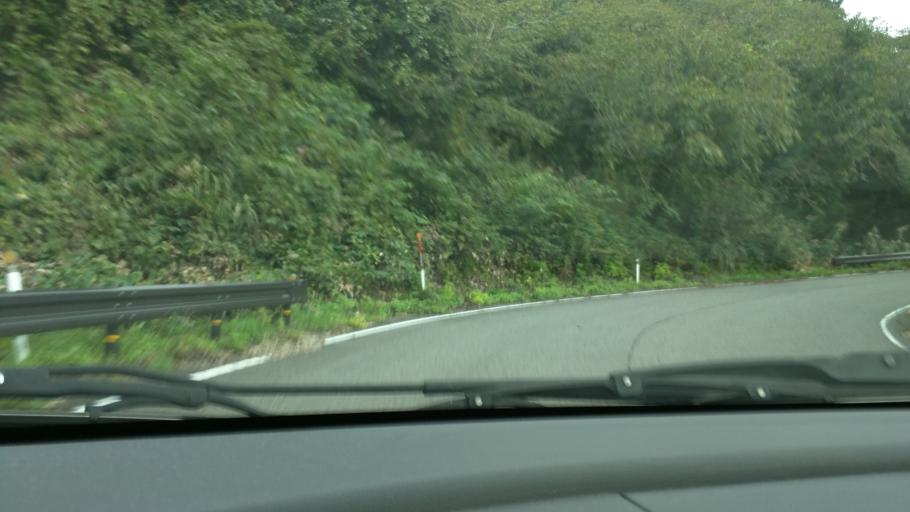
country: JP
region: Fukushima
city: Kitakata
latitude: 37.4581
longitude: 139.7187
